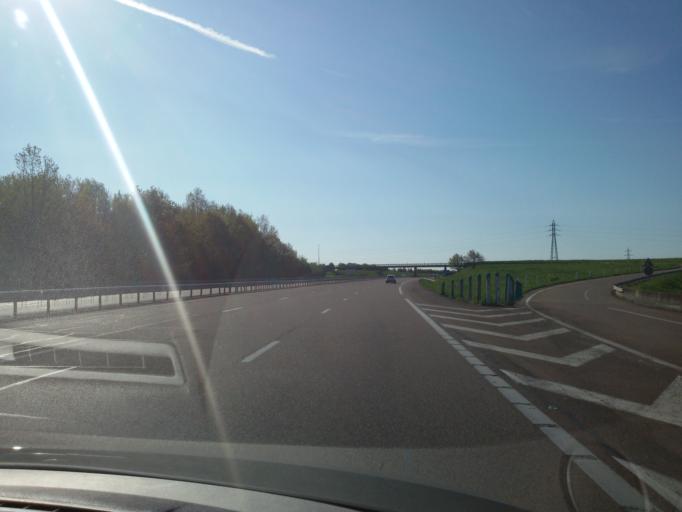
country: FR
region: Centre
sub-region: Departement du Loiret
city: Courtenay
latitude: 48.0492
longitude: 3.1097
